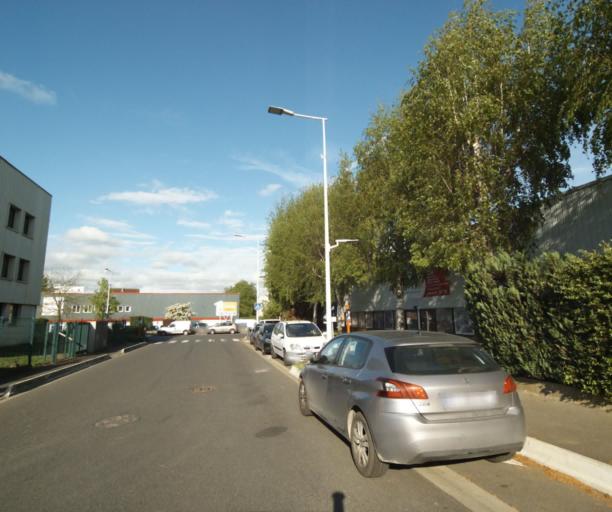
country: FR
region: Ile-de-France
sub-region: Departement de Seine-et-Marne
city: Torcy
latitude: 48.8447
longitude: 2.6568
